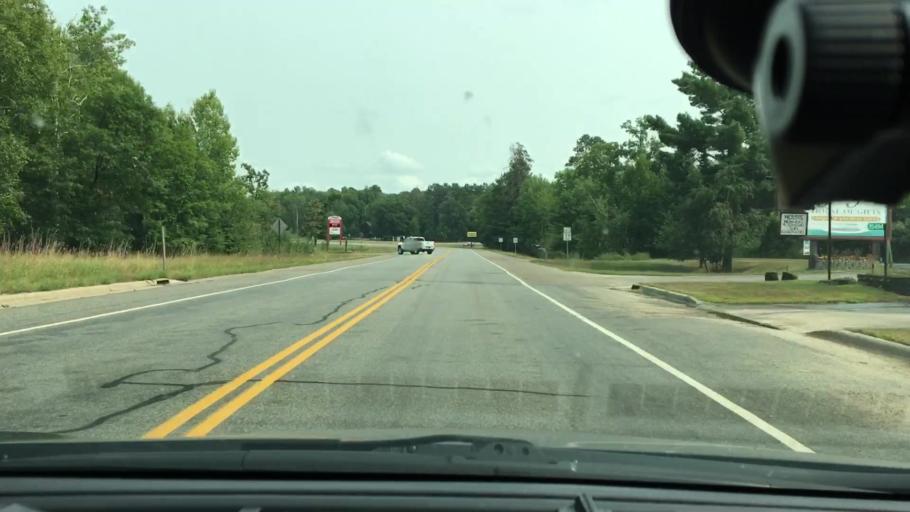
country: US
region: Minnesota
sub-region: Crow Wing County
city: Cross Lake
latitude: 46.6688
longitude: -94.1079
